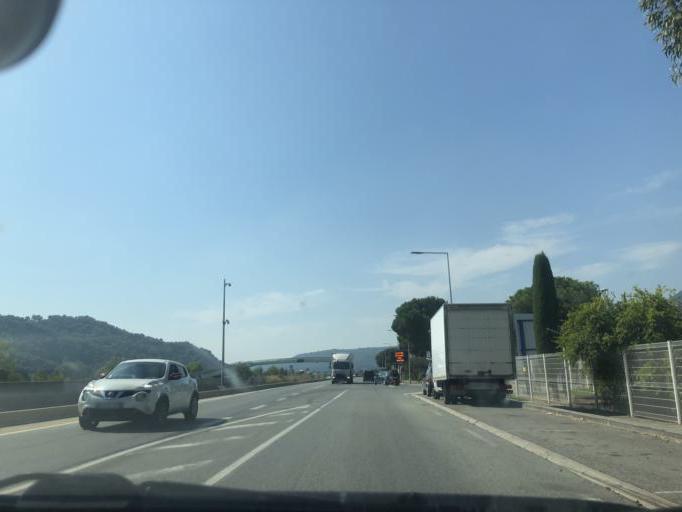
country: FR
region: Provence-Alpes-Cote d'Azur
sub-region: Departement des Alpes-Maritimes
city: Colomars
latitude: 43.7712
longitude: 7.2079
